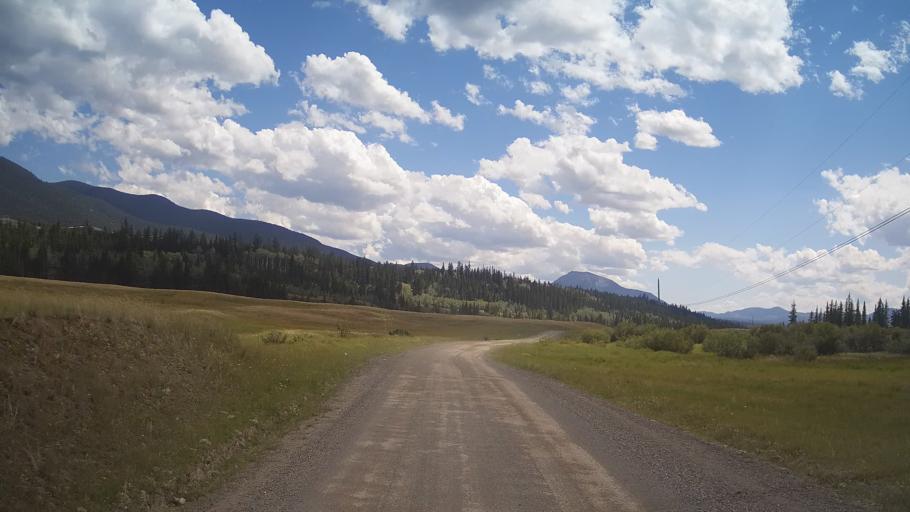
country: CA
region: British Columbia
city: Lillooet
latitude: 51.3235
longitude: -121.9804
